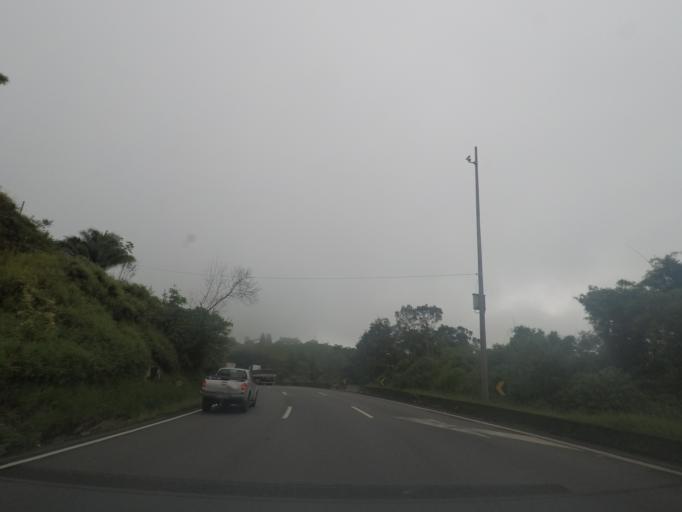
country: BR
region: Parana
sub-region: Antonina
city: Antonina
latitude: -25.0424
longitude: -48.5528
